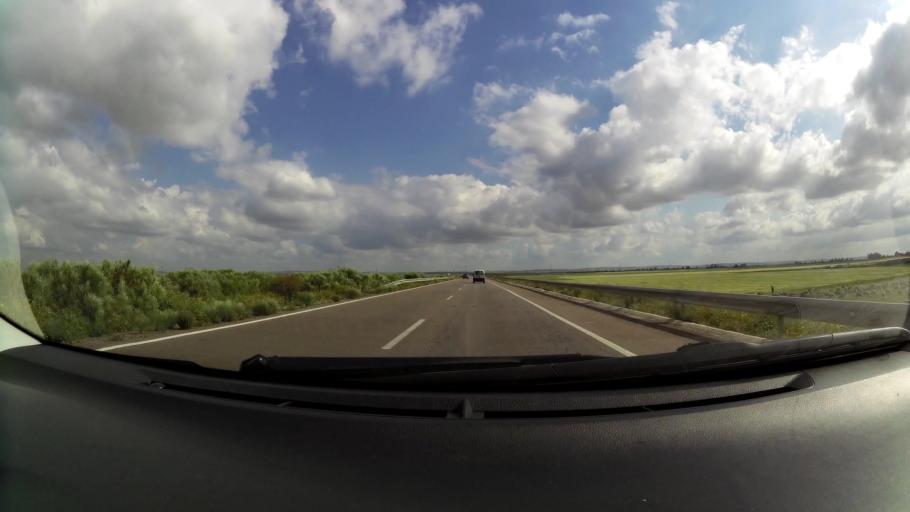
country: MA
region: Chaouia-Ouardigha
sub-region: Settat Province
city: Berrechid
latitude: 33.1883
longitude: -7.5750
